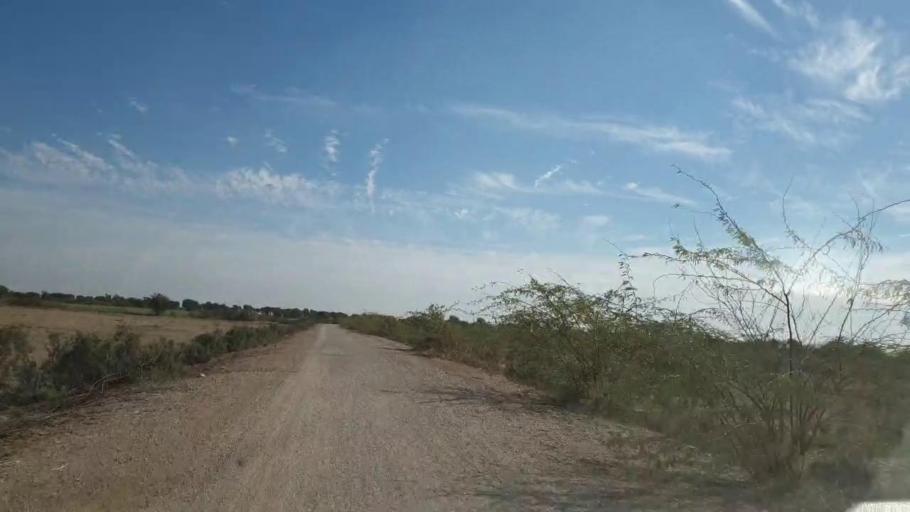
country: PK
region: Sindh
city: Pithoro
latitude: 25.5524
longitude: 69.2989
